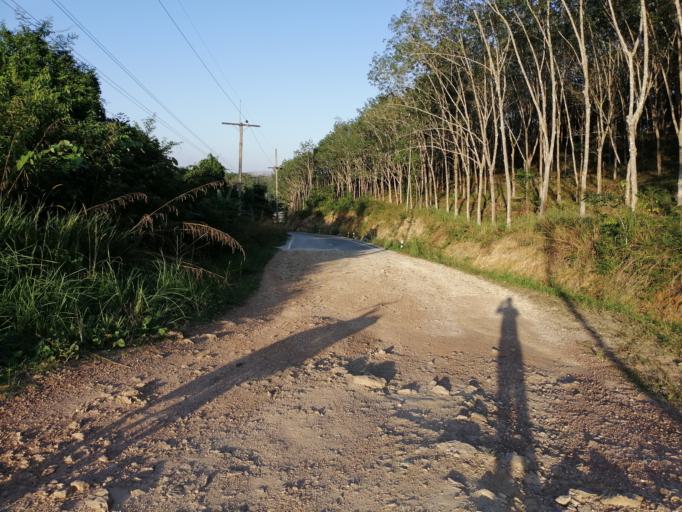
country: TH
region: Nakhon Si Thammarat
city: Chulabhorn
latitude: 7.9570
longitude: 99.8075
